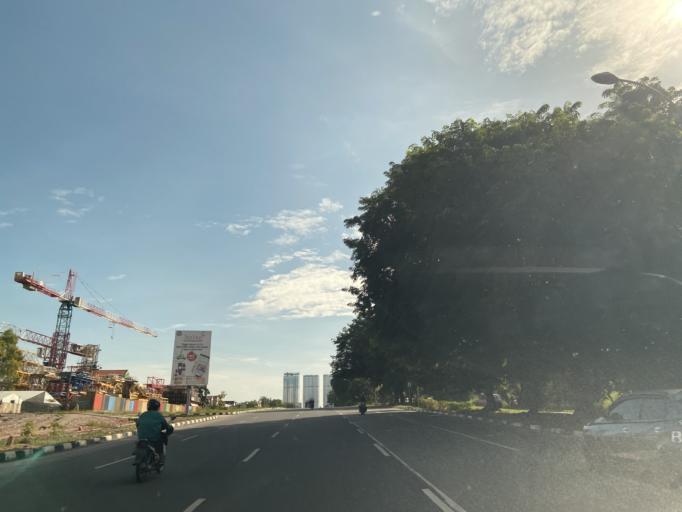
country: SG
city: Singapore
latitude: 1.1063
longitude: 104.0402
